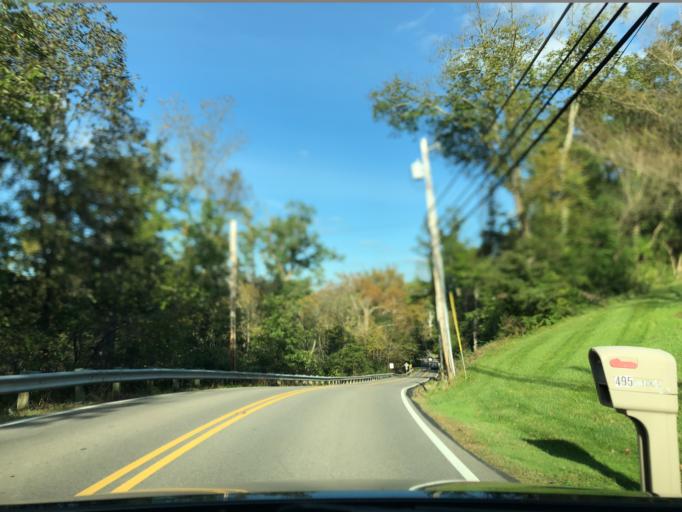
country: US
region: Ohio
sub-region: Hamilton County
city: The Village of Indian Hill
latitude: 39.2504
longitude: -84.2837
